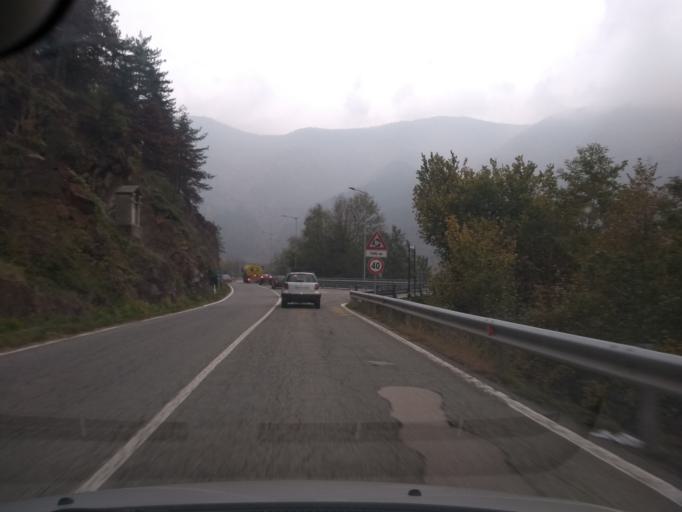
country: IT
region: Piedmont
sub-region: Provincia di Torino
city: Germagnano
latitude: 45.2617
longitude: 7.4596
